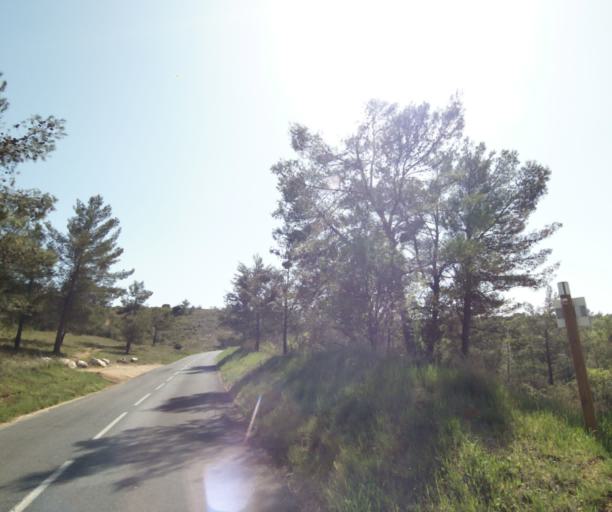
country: FR
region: Languedoc-Roussillon
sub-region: Departement de l'Herault
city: Grabels
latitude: 43.6482
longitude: 3.7774
